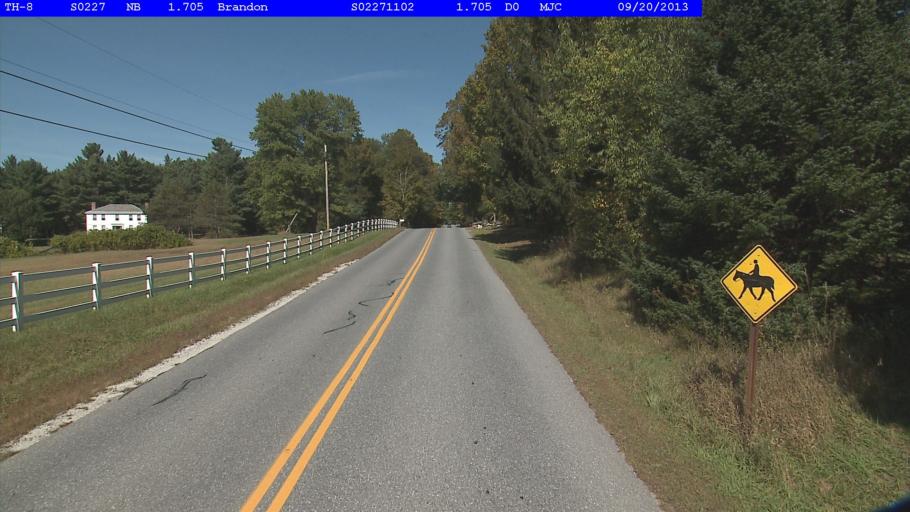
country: US
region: Vermont
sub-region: Rutland County
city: Brandon
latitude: 43.7990
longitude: -73.0551
